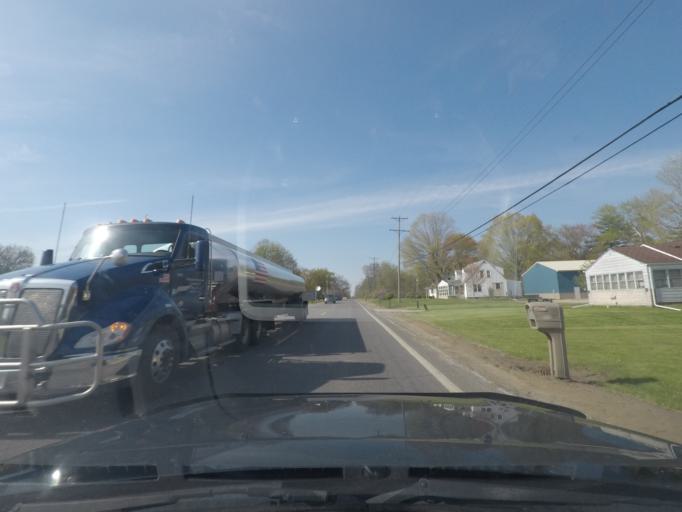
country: US
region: Michigan
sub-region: Berrien County
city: Niles
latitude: 41.7968
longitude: -86.2546
